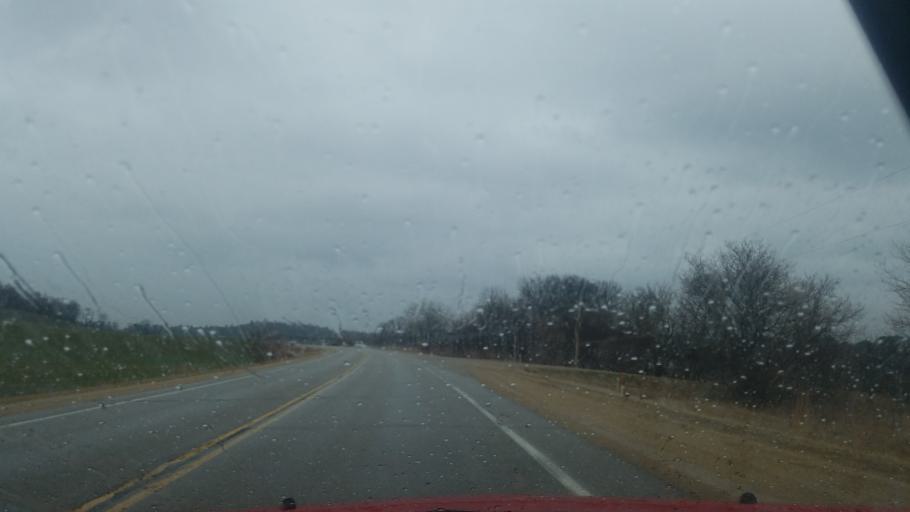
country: US
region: Wisconsin
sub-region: Dunn County
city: Tainter Lake
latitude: 44.9594
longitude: -91.8958
